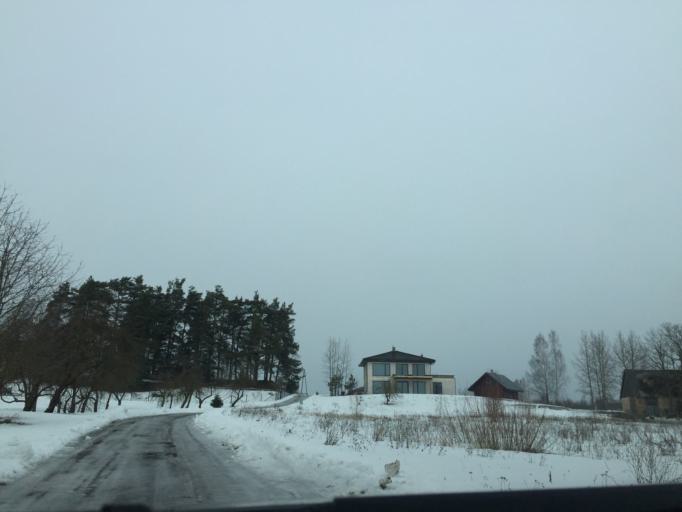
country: LV
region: Ikskile
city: Ikskile
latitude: 56.8430
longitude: 24.4594
